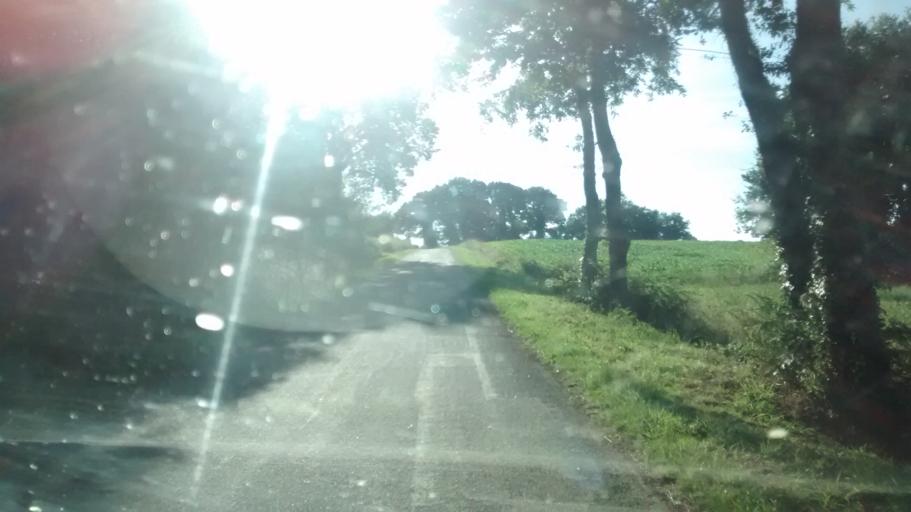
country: FR
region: Brittany
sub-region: Departement du Morbihan
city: Molac
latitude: 47.7160
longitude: -2.4541
